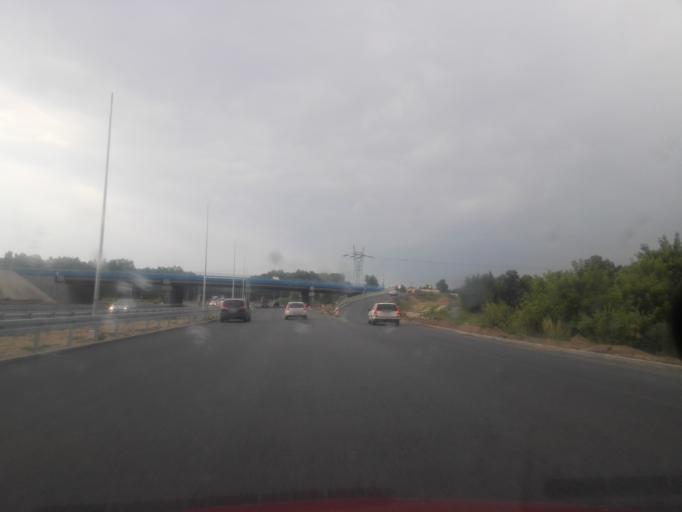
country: PL
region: Silesian Voivodeship
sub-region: Czestochowa
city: Czestochowa
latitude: 50.8291
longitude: 19.1451
